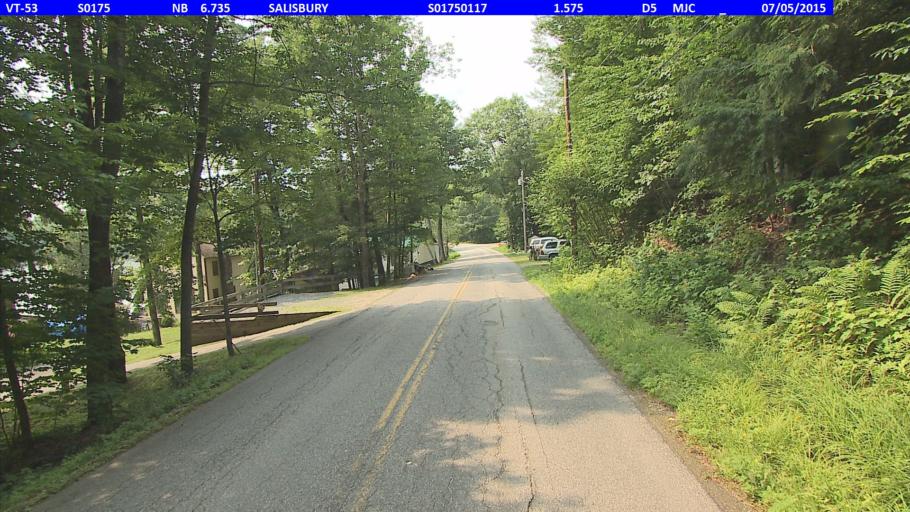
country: US
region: Vermont
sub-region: Rutland County
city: Brandon
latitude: 43.9198
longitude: -73.0707
